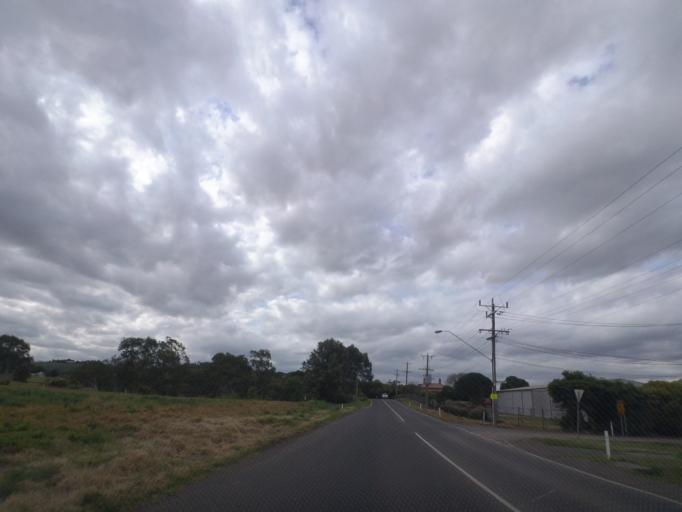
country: AU
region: Victoria
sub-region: Brimbank
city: Keilor
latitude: -37.7075
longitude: 144.8321
